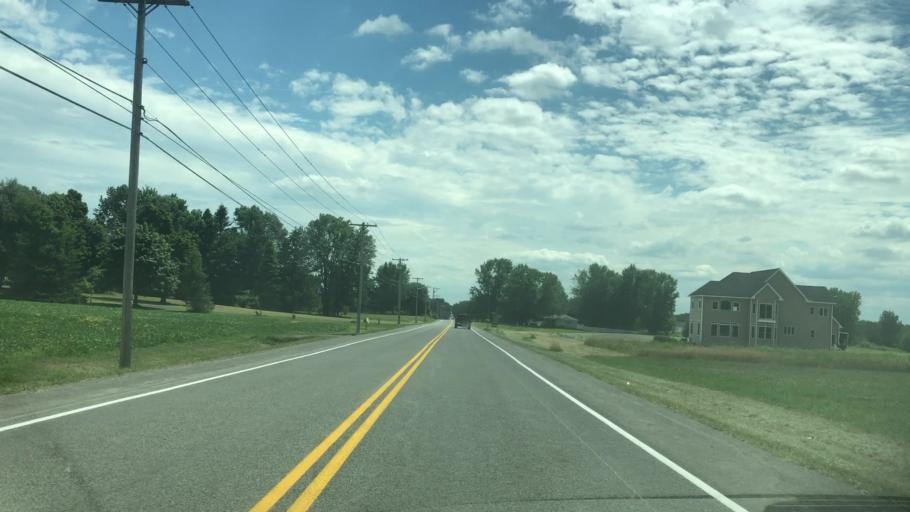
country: US
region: New York
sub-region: Monroe County
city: Webster
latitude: 43.1567
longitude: -77.4006
